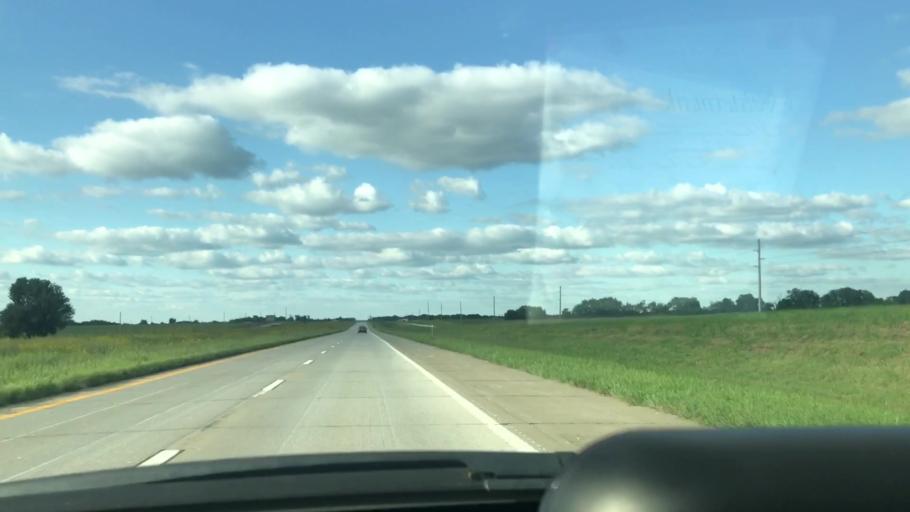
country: US
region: Missouri
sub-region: Benton County
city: Cole Camp
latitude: 38.5096
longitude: -93.2728
